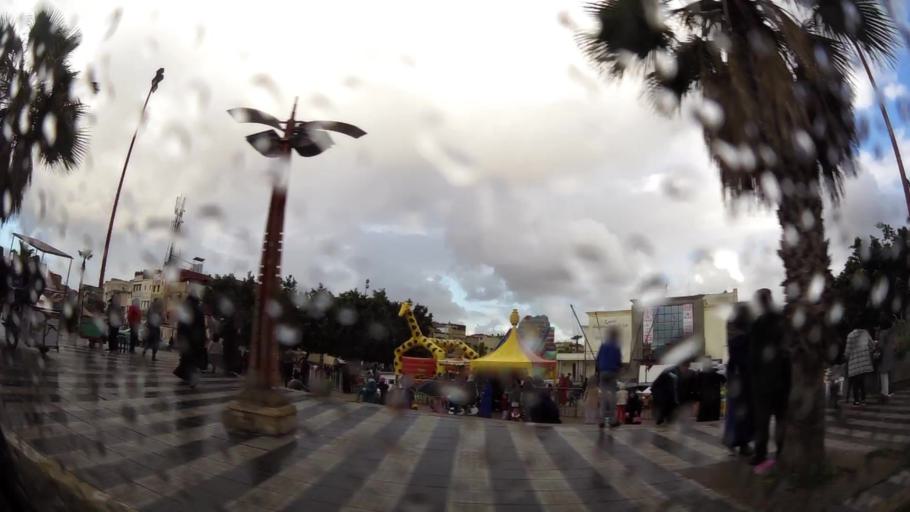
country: MA
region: Grand Casablanca
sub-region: Mohammedia
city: Mohammedia
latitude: 33.6860
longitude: -7.3900
